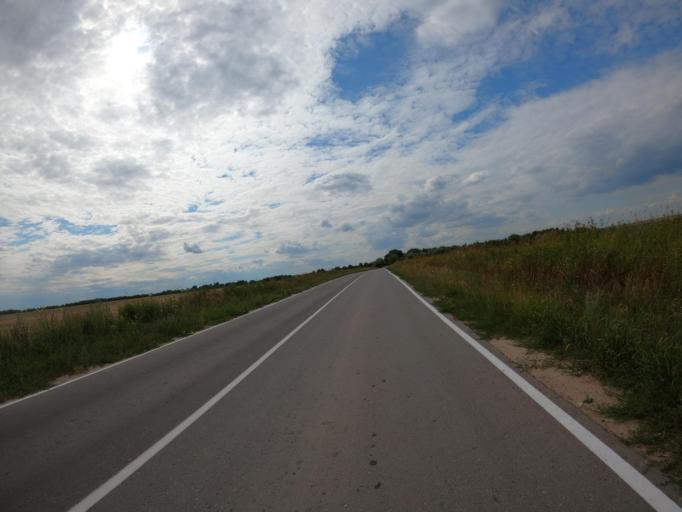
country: RU
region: Moskovskaya
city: Bronnitsy
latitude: 55.4872
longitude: 38.2491
